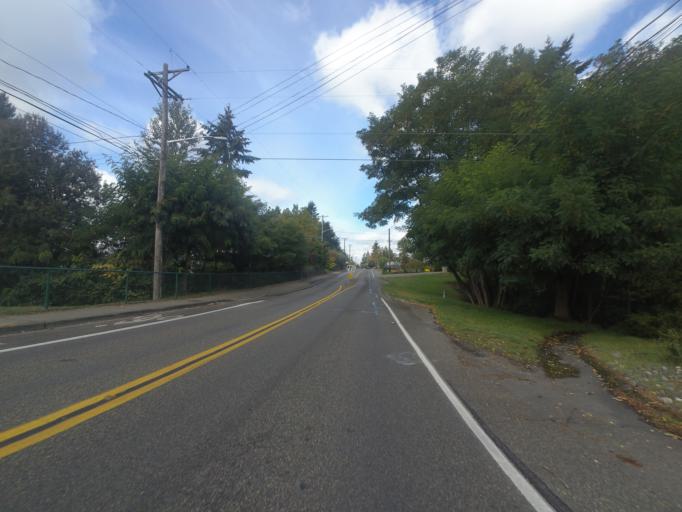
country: US
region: Washington
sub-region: Pierce County
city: University Place
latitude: 47.2243
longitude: -122.5449
